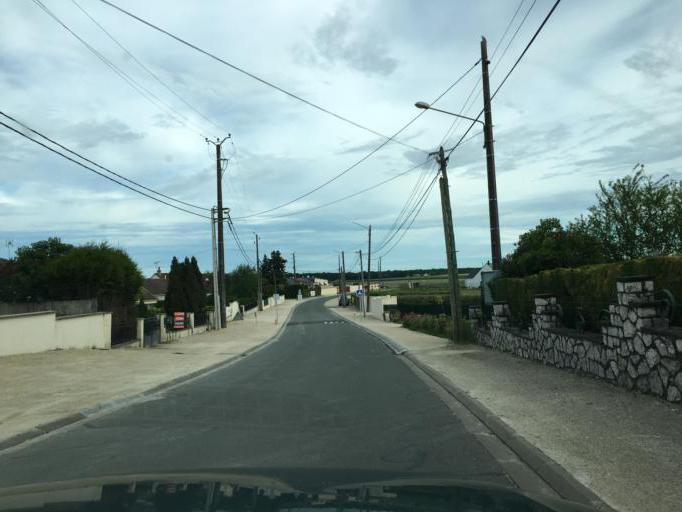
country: FR
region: Centre
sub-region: Departement du Loiret
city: Chaingy
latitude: 47.9365
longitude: 1.7640
